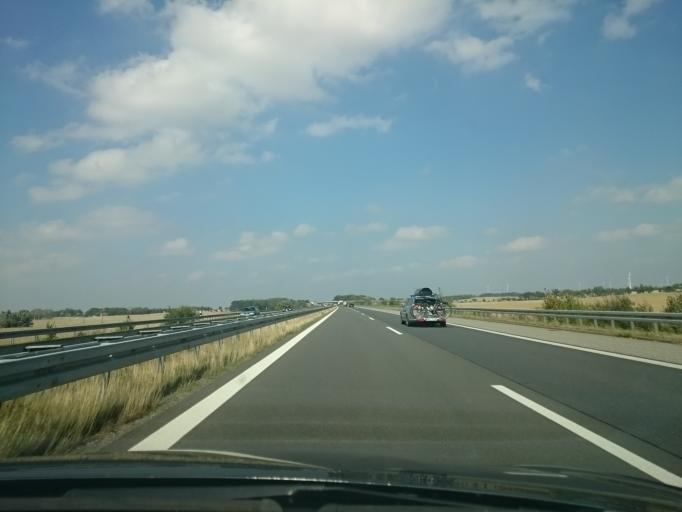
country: DE
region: Brandenburg
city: Schonfeld
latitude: 53.3980
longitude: 13.9944
